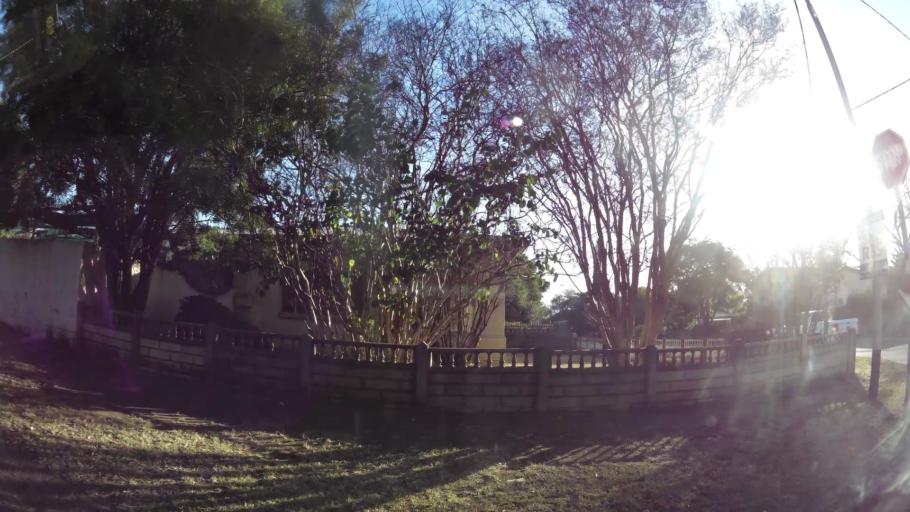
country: ZA
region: Gauteng
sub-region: City of Tshwane Metropolitan Municipality
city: Pretoria
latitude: -25.7155
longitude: 28.2098
